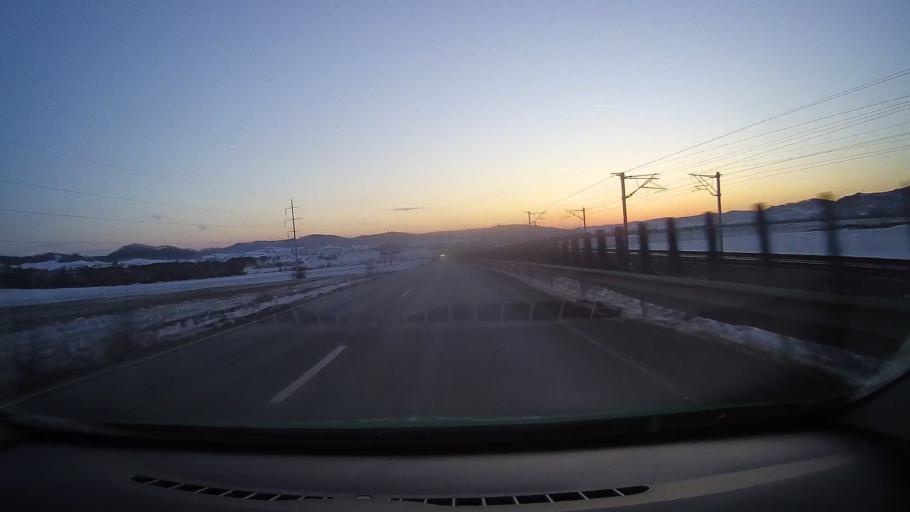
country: RO
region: Sibiu
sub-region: Comuna Brateiu
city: Brateiu
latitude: 46.1853
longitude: 24.4473
